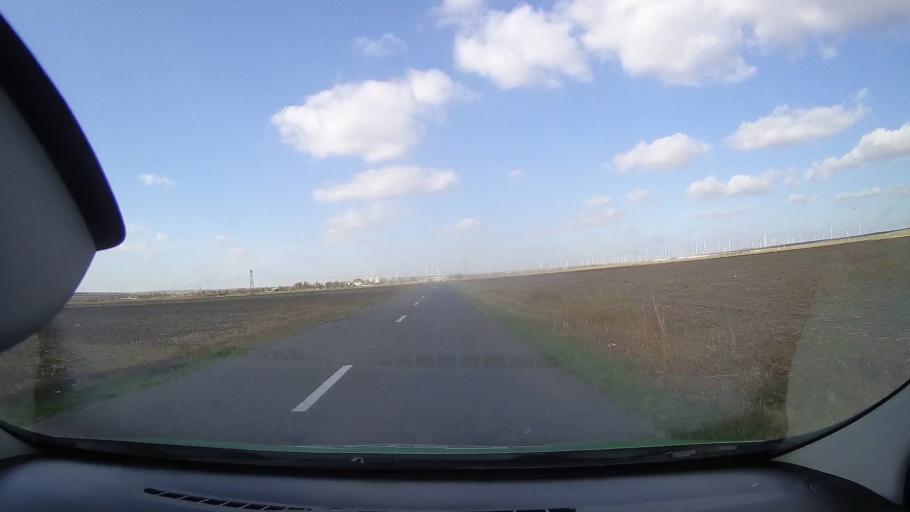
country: RO
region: Constanta
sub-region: Comuna Cogealac
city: Tariverde
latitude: 44.5549
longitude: 28.6193
